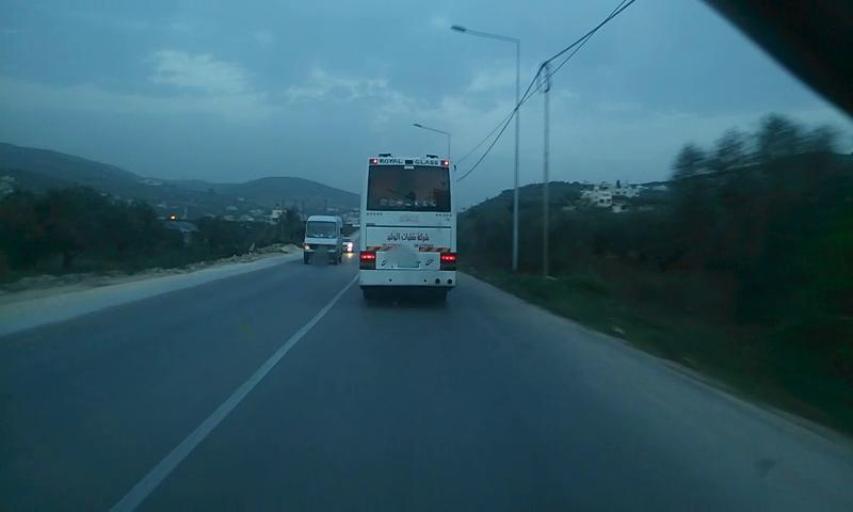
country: PS
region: West Bank
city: Kafr al Labad
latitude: 32.3116
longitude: 35.0980
